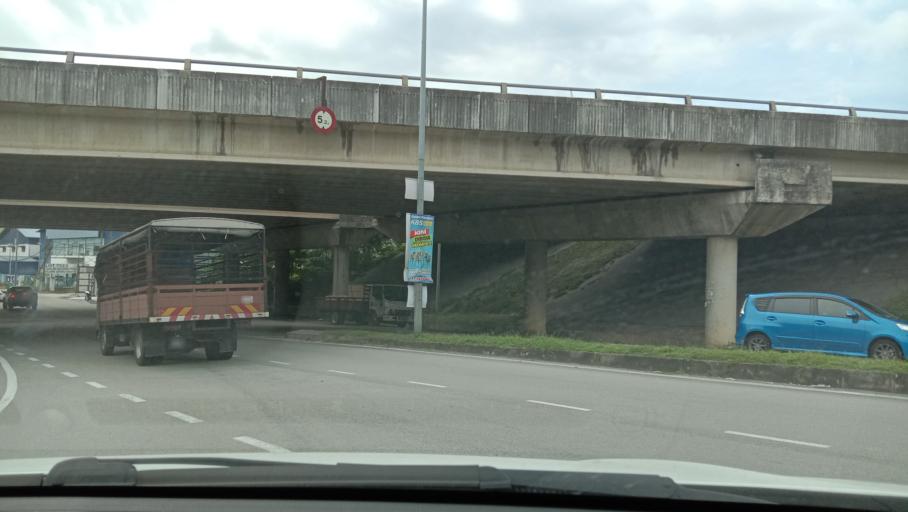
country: MY
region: Selangor
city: Kampung Baru Subang
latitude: 3.1376
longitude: 101.5254
